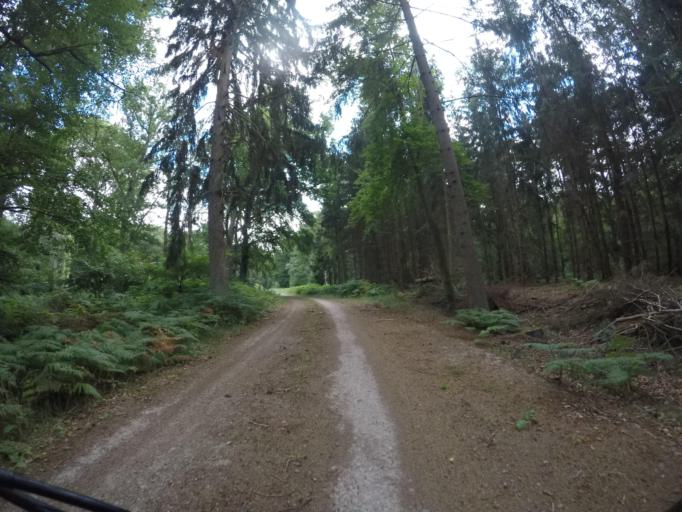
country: DE
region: Mecklenburg-Vorpommern
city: Lubtheen
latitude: 53.2811
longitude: 10.9818
